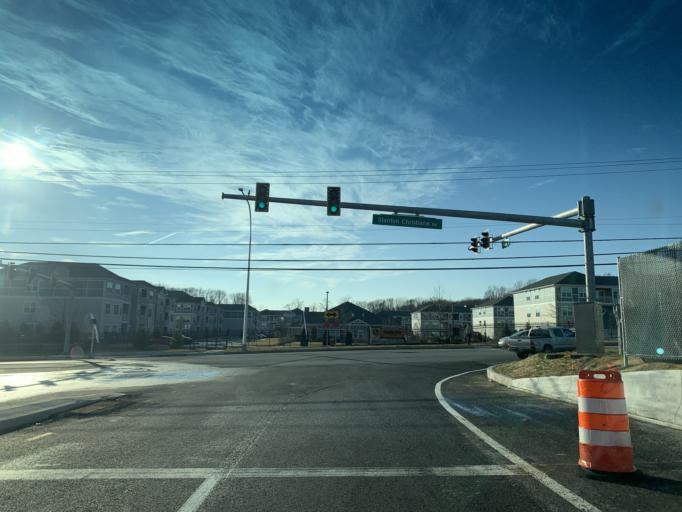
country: US
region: Delaware
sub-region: New Castle County
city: Bear
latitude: 39.6743
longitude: -75.6576
